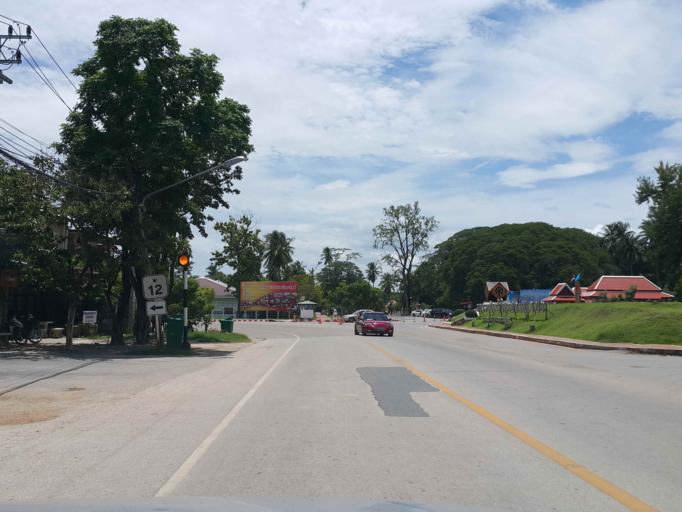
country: TH
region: Sukhothai
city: Ban Na
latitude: 17.0193
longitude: 99.7068
